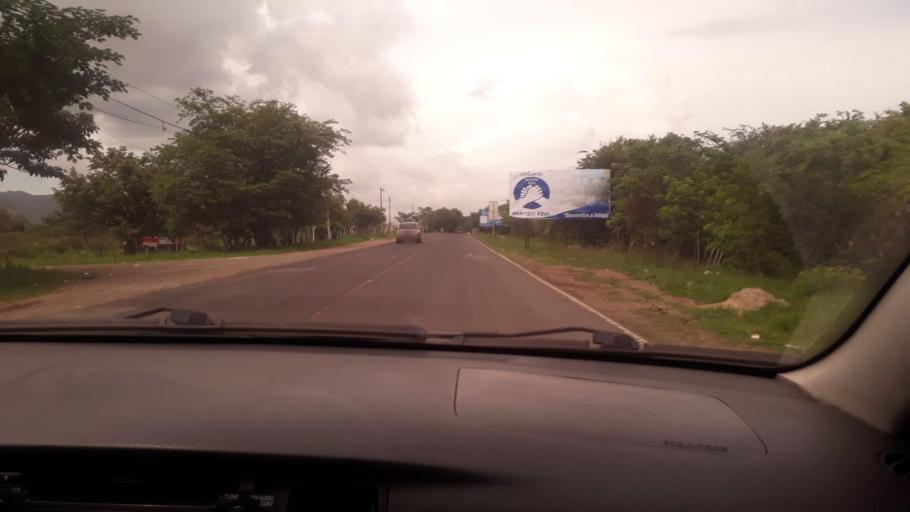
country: GT
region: Jutiapa
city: Jutiapa
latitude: 14.2866
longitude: -89.9429
